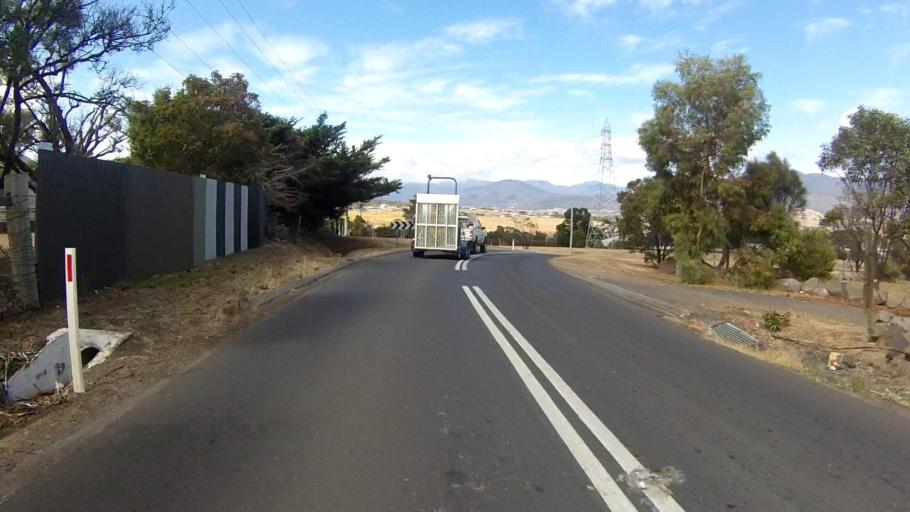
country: AU
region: Tasmania
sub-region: Brighton
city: Old Beach
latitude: -42.7500
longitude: 147.2799
